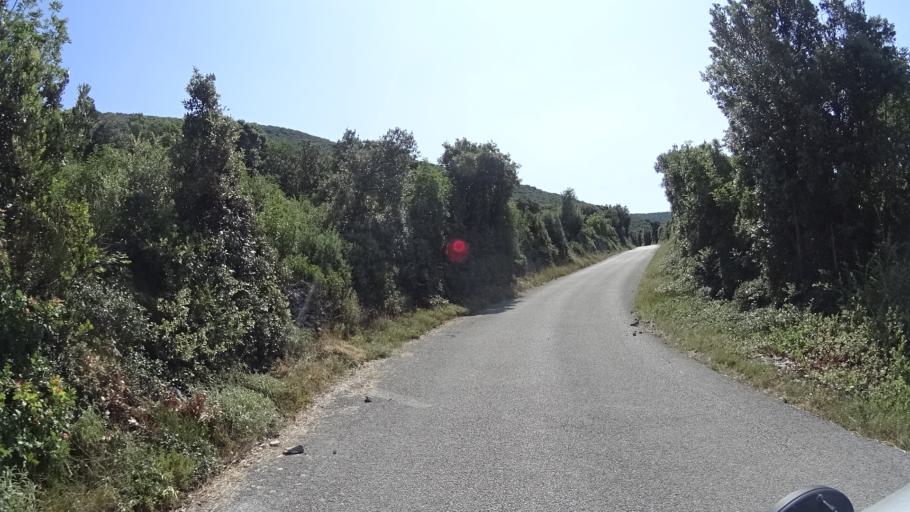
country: HR
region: Istarska
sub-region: Grad Labin
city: Rabac
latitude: 44.9782
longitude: 14.1296
